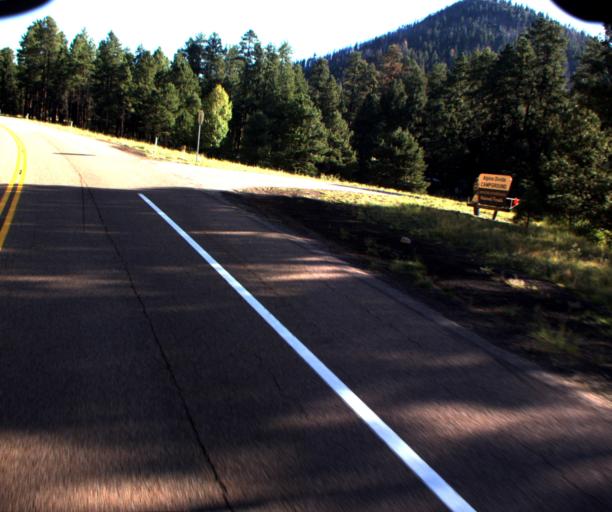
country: US
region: Arizona
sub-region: Apache County
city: Eagar
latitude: 33.8940
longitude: -109.1544
